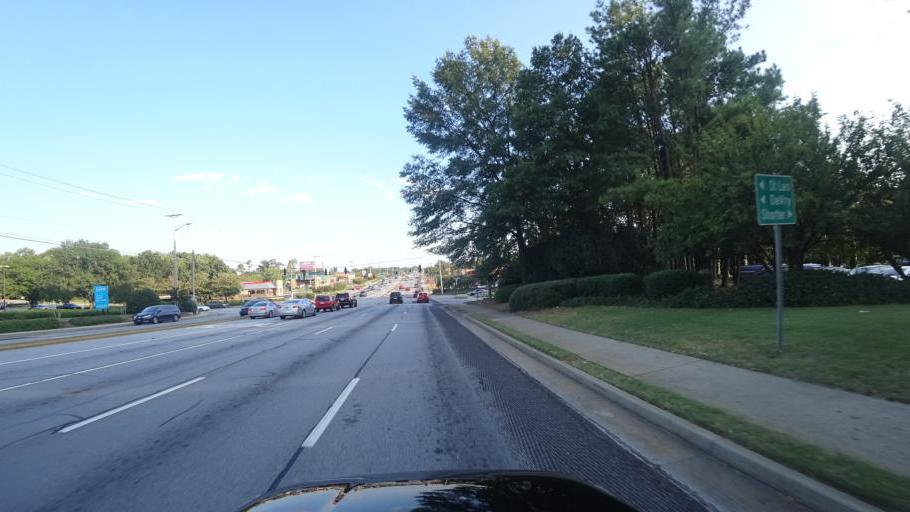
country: US
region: Georgia
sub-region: Gwinnett County
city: Duluth
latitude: 33.9480
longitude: -84.1272
